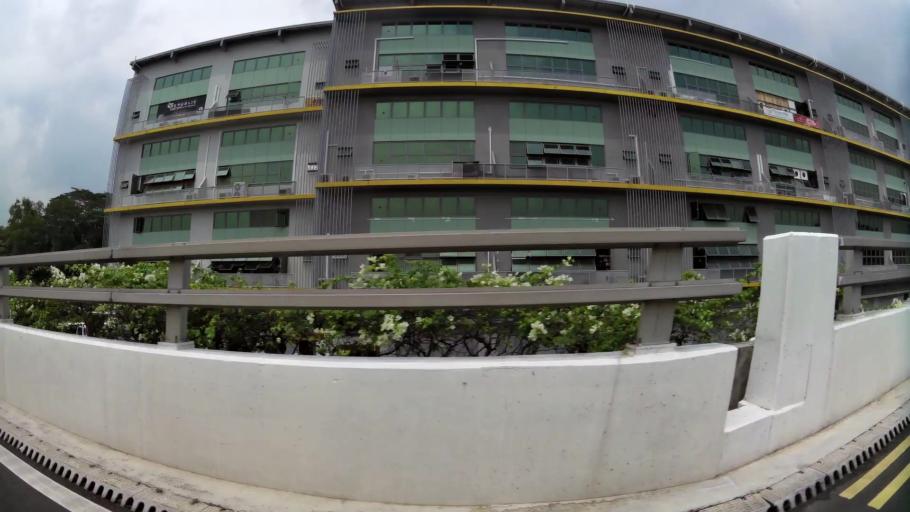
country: SG
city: Singapore
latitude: 1.3406
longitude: 103.9147
